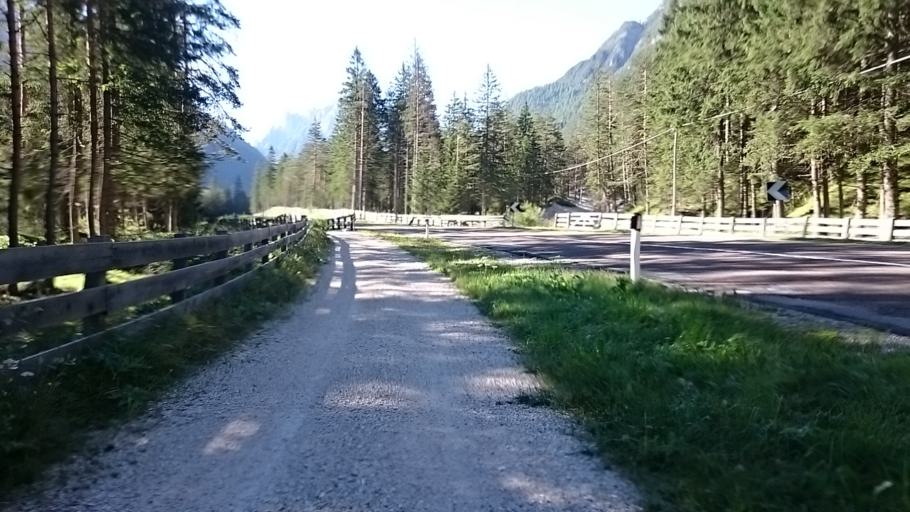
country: IT
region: Trentino-Alto Adige
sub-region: Bolzano
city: Dobbiaco
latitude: 46.6612
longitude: 12.2238
